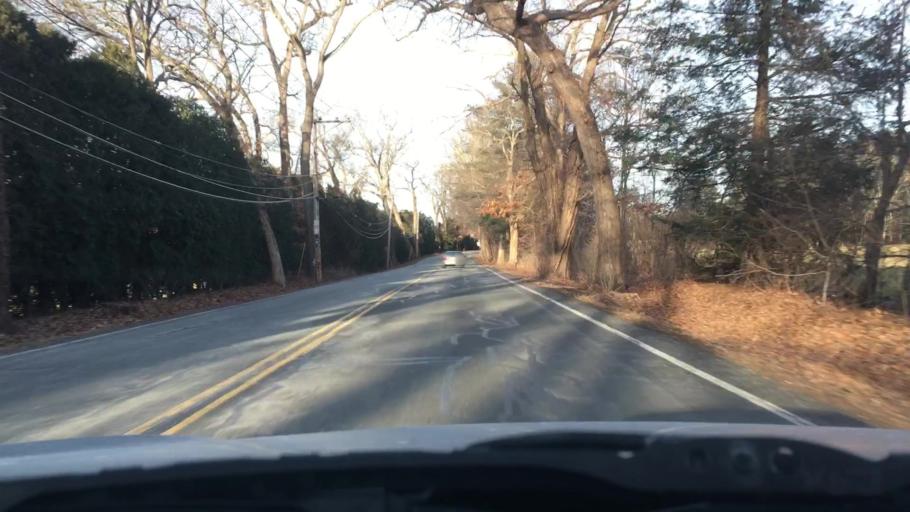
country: US
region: Massachusetts
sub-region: Hampden County
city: Longmeadow
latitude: 42.0392
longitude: -72.5670
